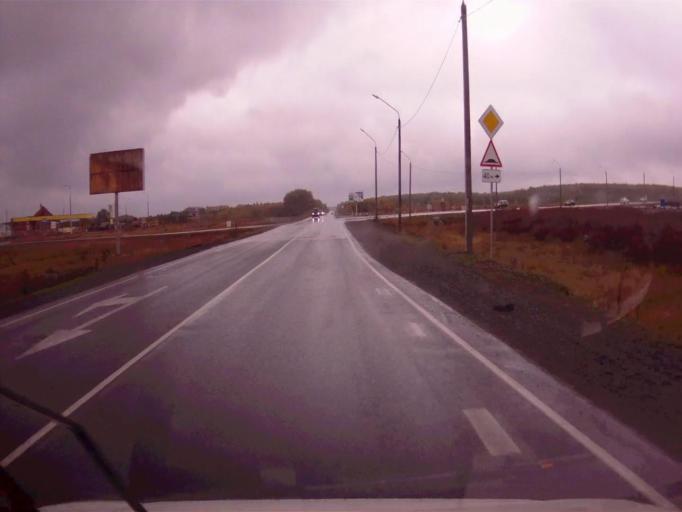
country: RU
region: Chelyabinsk
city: Tayginka
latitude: 55.4997
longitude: 60.6373
